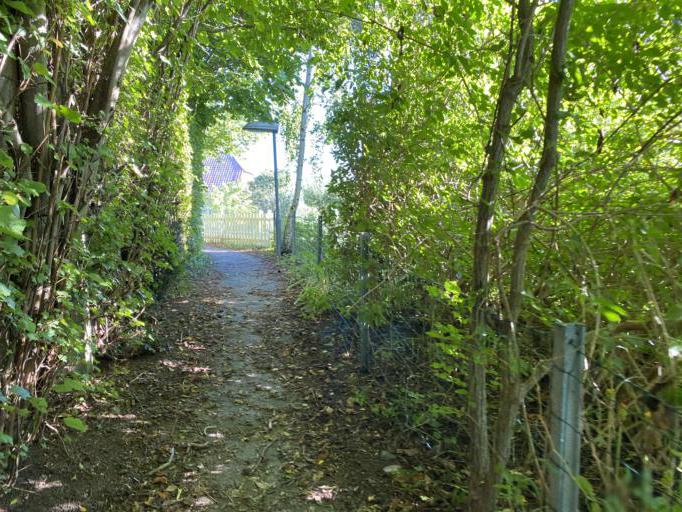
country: DK
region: Zealand
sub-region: Guldborgsund Kommune
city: Sakskobing
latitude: 54.9800
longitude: 11.5355
